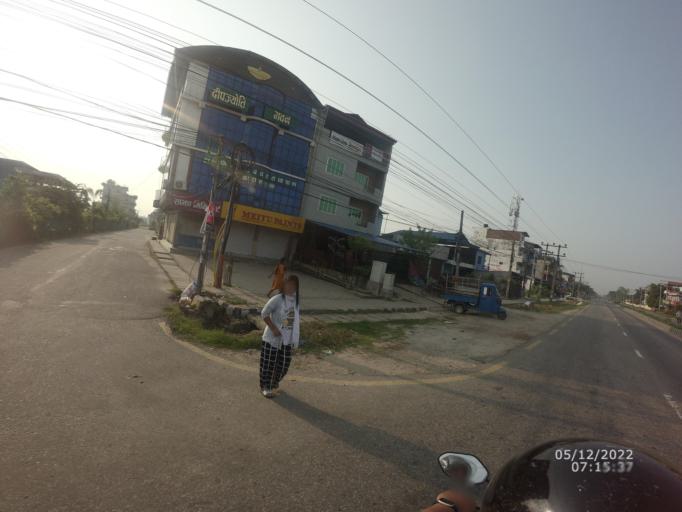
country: NP
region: Central Region
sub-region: Narayani Zone
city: Bharatpur
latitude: 27.6870
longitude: 84.4400
